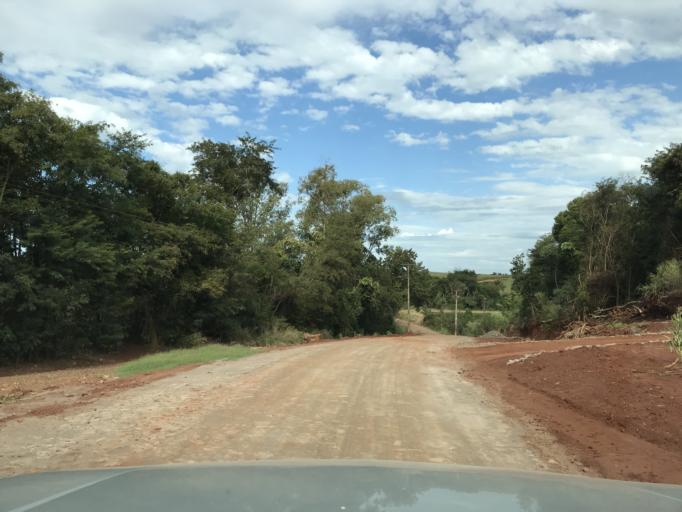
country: BR
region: Parana
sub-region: Palotina
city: Palotina
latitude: -24.3012
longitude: -53.8103
